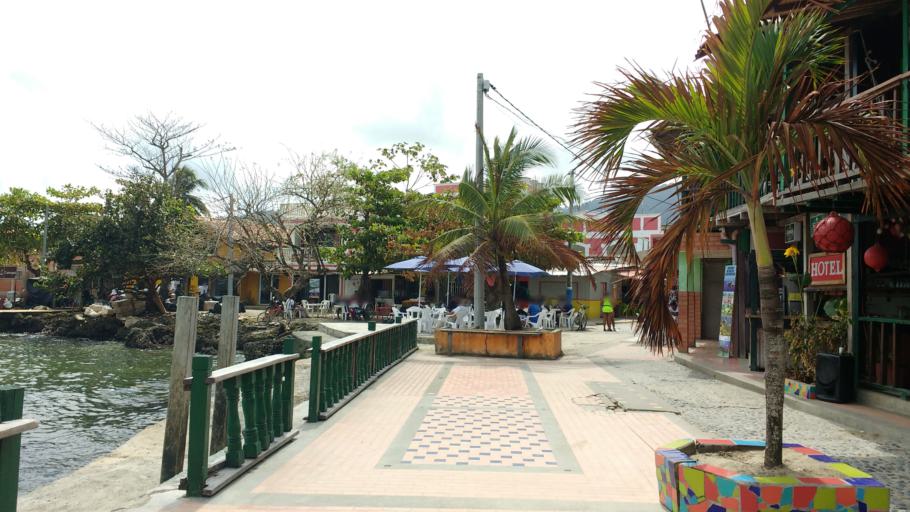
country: PA
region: Guna Yala
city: Puerto Obaldia
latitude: 8.6383
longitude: -77.3467
